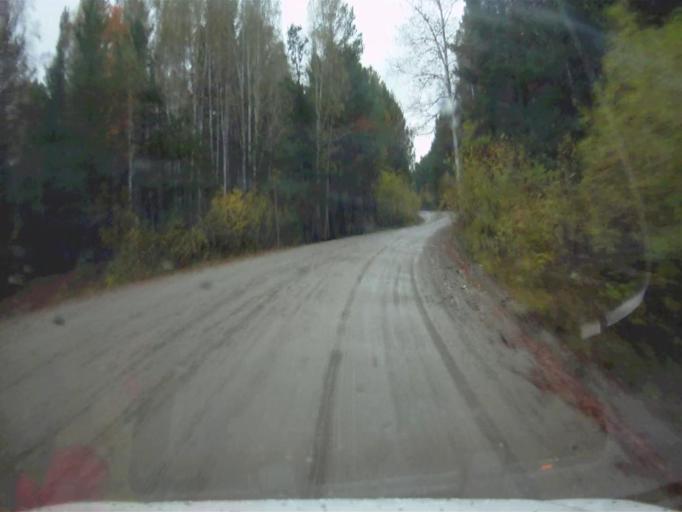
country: RU
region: Chelyabinsk
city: Kyshtym
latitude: 55.8346
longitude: 60.4856
